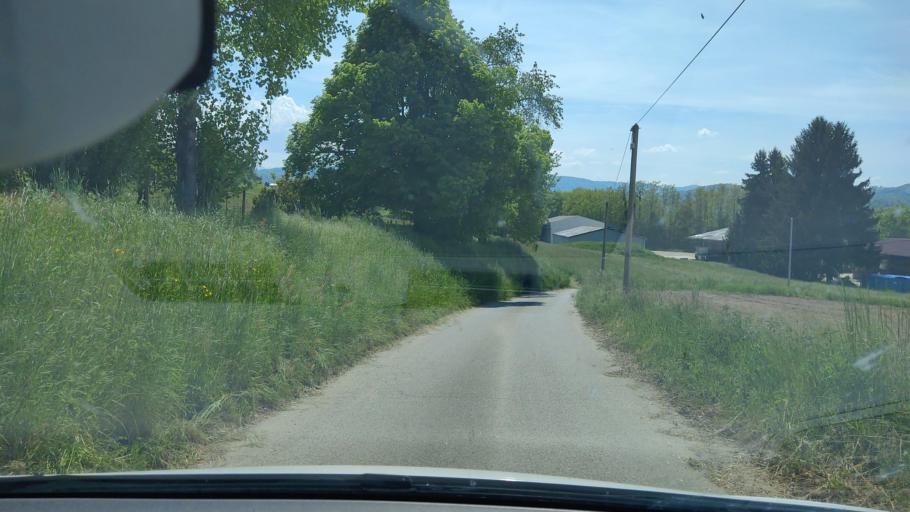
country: FR
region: Rhone-Alpes
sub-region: Departement de la Savoie
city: Domessin
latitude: 45.5223
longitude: 5.7162
